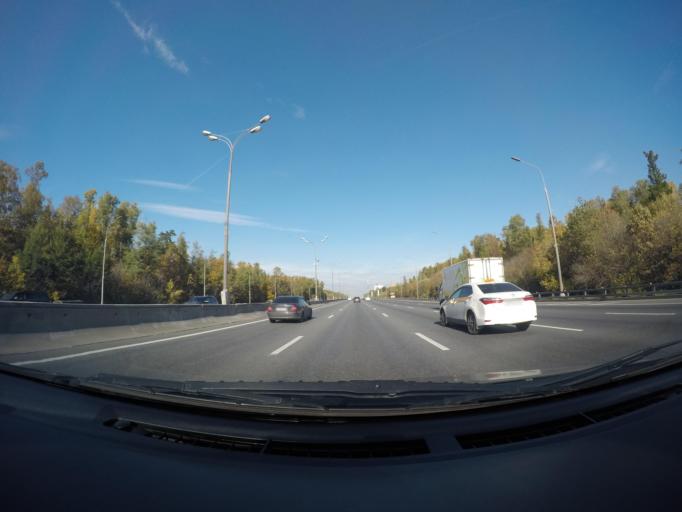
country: RU
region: Moscow
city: Ivanovskoye
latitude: 55.7902
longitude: 37.8414
